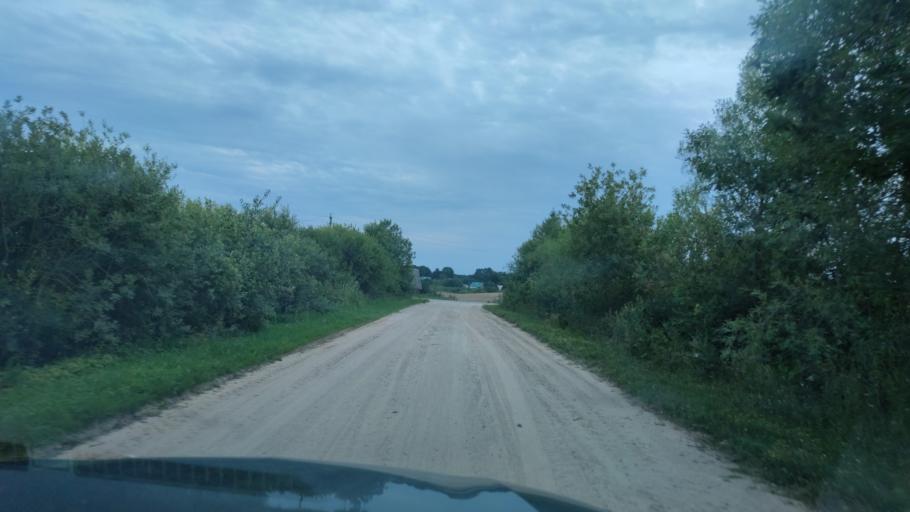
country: BY
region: Minsk
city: Myadzyel
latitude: 55.0903
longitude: 27.1295
